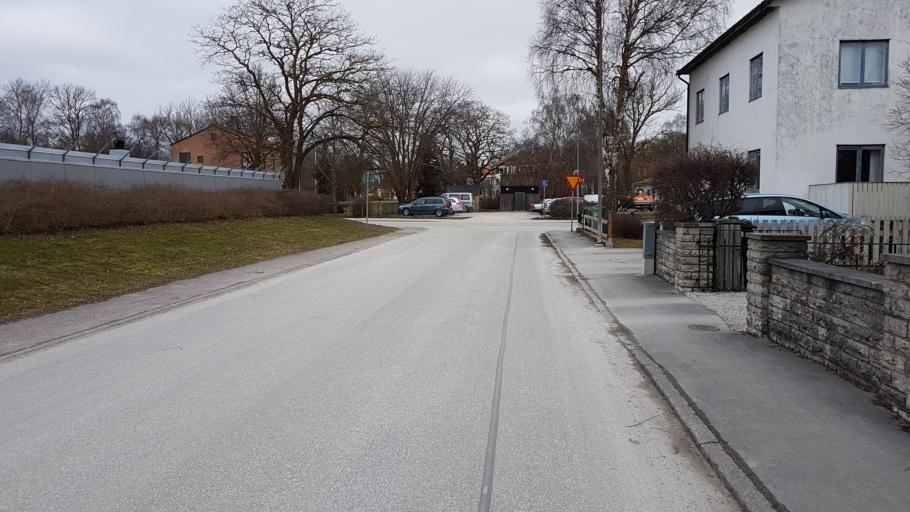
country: SE
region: Gotland
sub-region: Gotland
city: Visby
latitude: 57.6373
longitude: 18.3064
